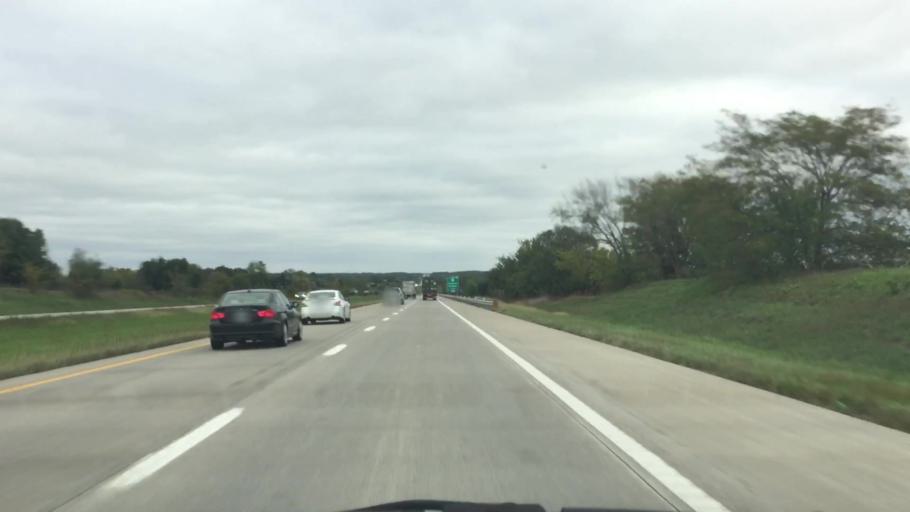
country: US
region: Missouri
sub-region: Clinton County
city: Cameron
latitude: 39.6481
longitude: -94.2399
